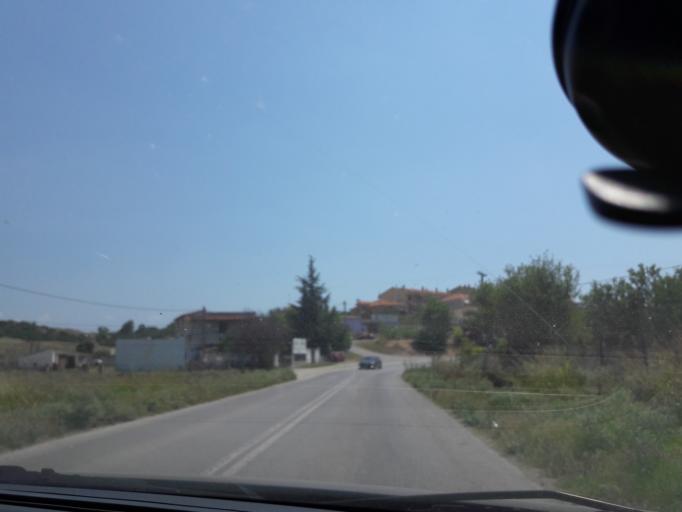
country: GR
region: Central Macedonia
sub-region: Nomos Chalkidikis
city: Nea Kallikrateia
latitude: 40.3242
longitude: 23.0661
